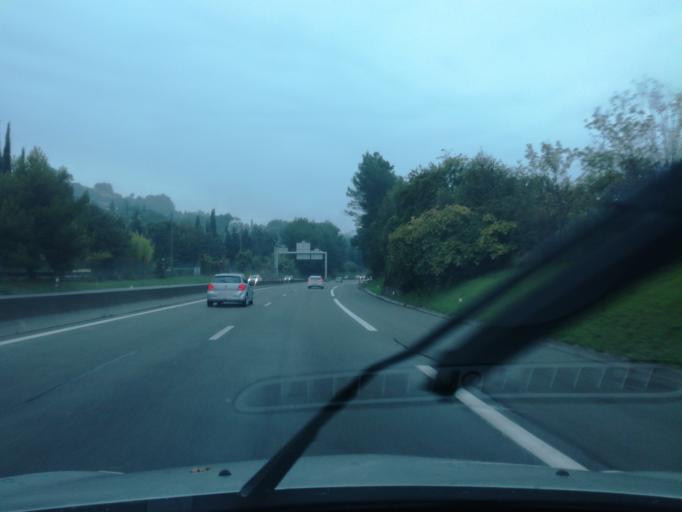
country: FR
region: Provence-Alpes-Cote d'Azur
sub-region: Departement des Alpes-Maritimes
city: Mougins
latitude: 43.5934
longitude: 7.0000
